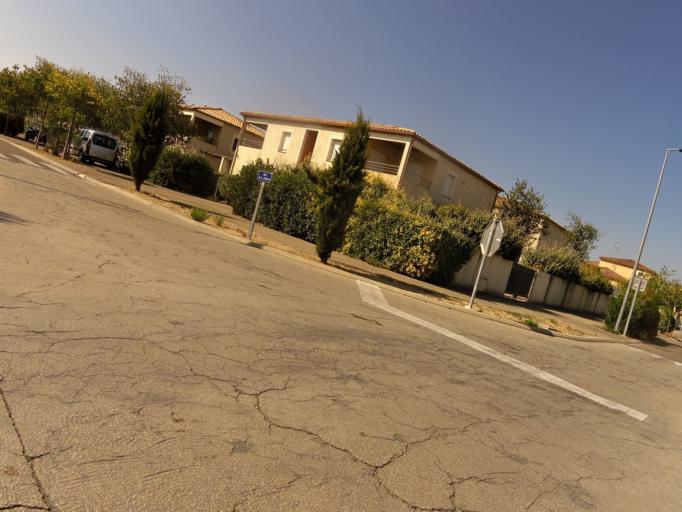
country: FR
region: Languedoc-Roussillon
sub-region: Departement du Gard
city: Calvisson
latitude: 43.7852
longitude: 4.2001
